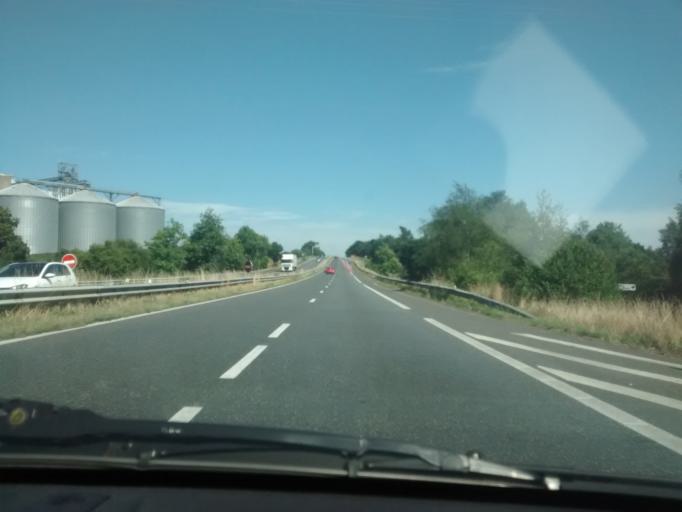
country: FR
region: Brittany
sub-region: Departement des Cotes-d'Armor
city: Plouagat
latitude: 48.5298
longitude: -2.9706
